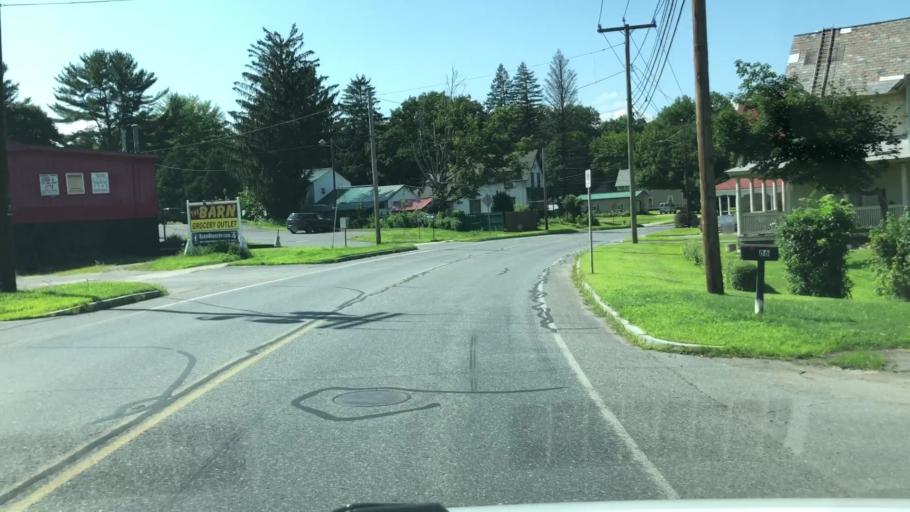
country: US
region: Massachusetts
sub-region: Franklin County
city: Greenfield
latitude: 42.5828
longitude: -72.6106
